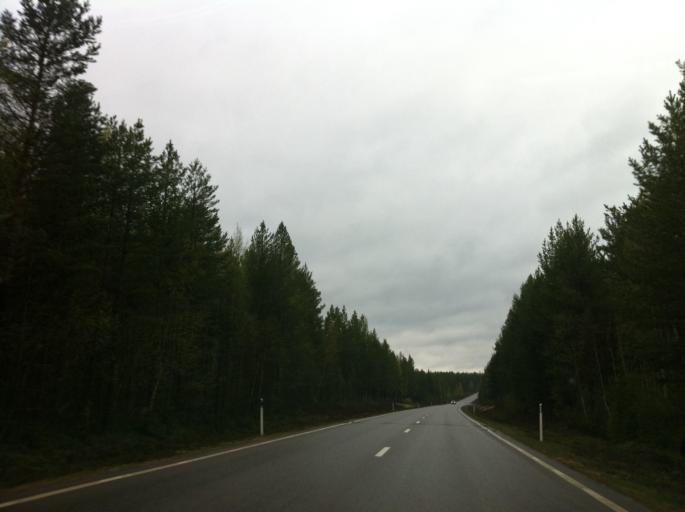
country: SE
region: Jaemtland
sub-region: Harjedalens Kommun
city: Sveg
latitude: 62.1090
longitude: 14.1916
